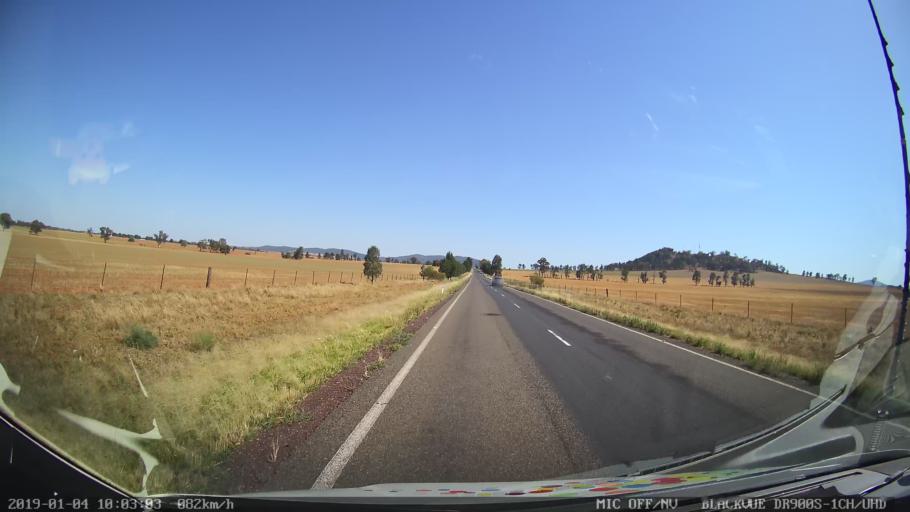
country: AU
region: New South Wales
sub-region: Cabonne
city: Canowindra
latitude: -33.4686
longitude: 148.3648
